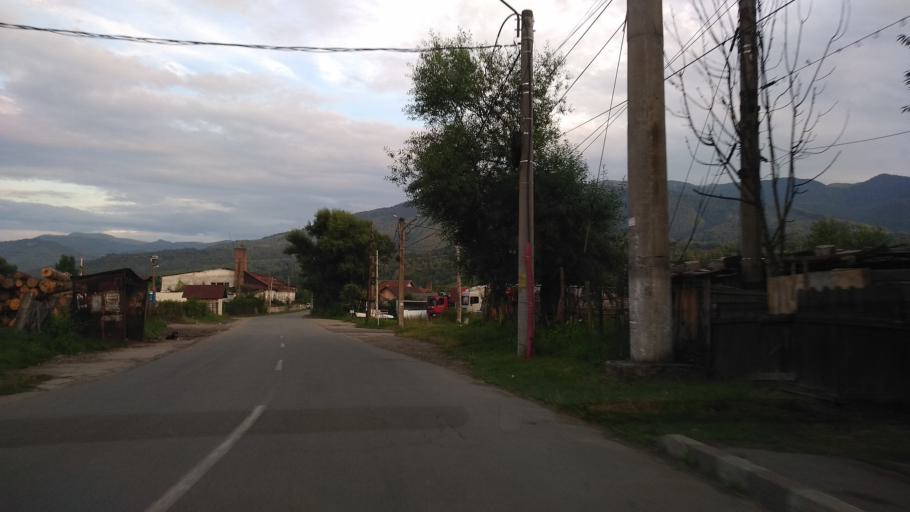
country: RO
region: Hunedoara
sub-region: Comuna Aninoasa
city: Iscroni
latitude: 45.3845
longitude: 23.3273
